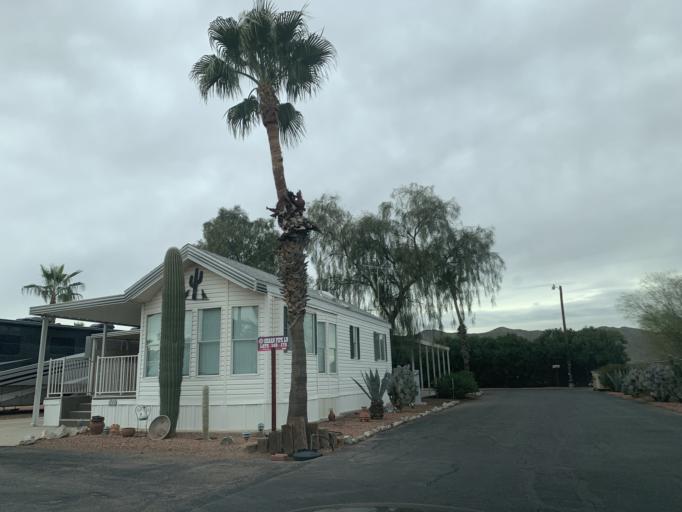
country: US
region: Arizona
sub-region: Pinal County
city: Arizona City
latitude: 32.8154
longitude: -111.6752
